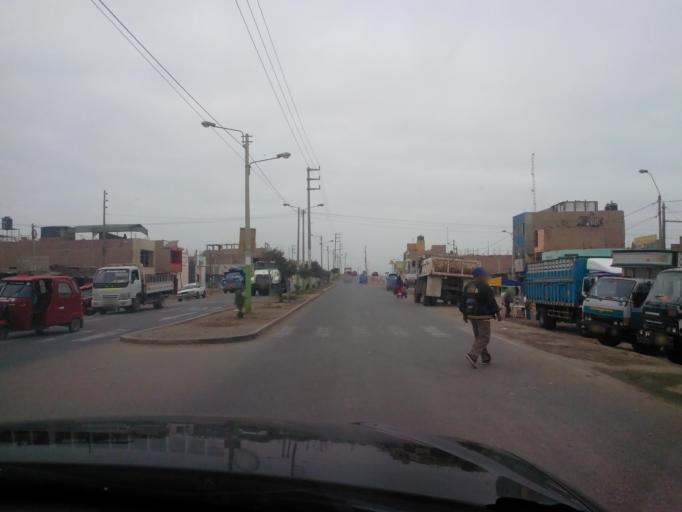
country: PE
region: Ica
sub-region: Provincia de Pisco
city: San Clemente
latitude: -13.6815
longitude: -76.1550
